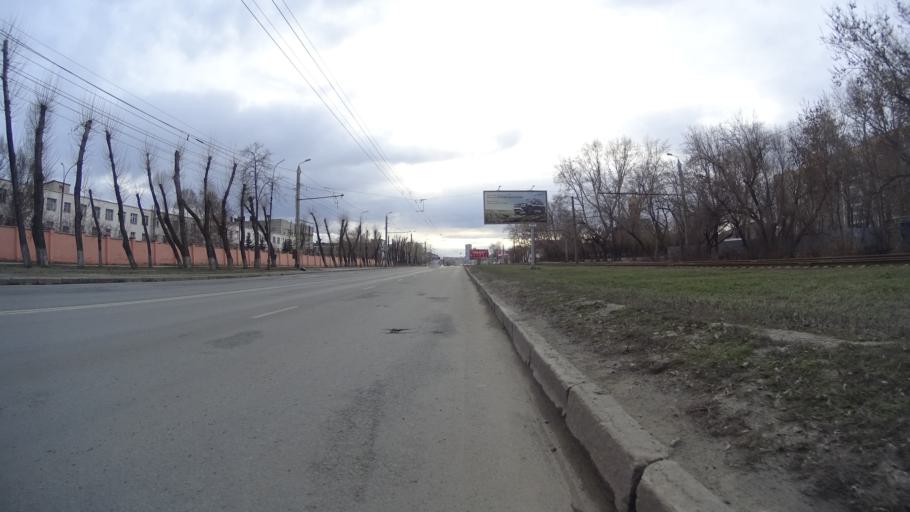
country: RU
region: Chelyabinsk
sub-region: Gorod Chelyabinsk
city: Chelyabinsk
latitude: 55.1598
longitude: 61.4574
